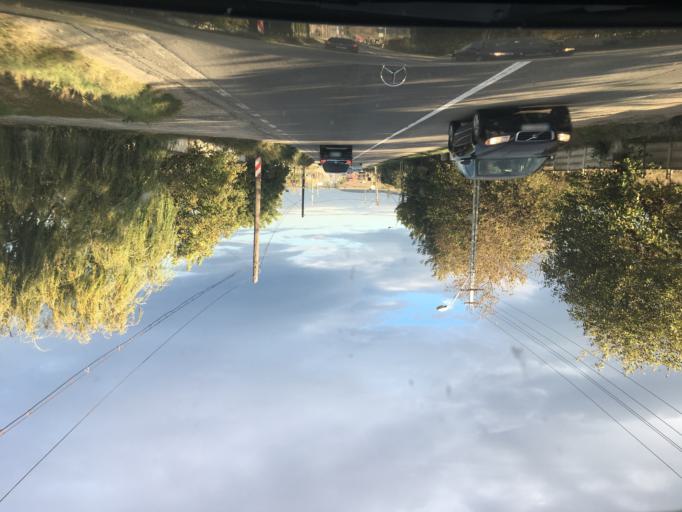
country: RO
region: Alba
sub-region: Oras Teius
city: Teius
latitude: 46.2142
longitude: 23.6778
